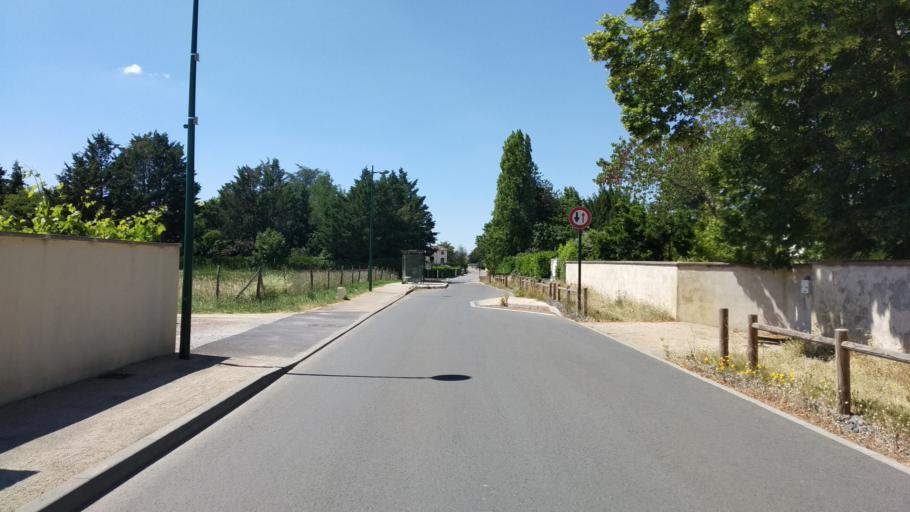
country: FR
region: Poitou-Charentes
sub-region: Departement de la Vienne
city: Vouneuil-sous-Biard
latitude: 46.6029
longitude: 0.2840
